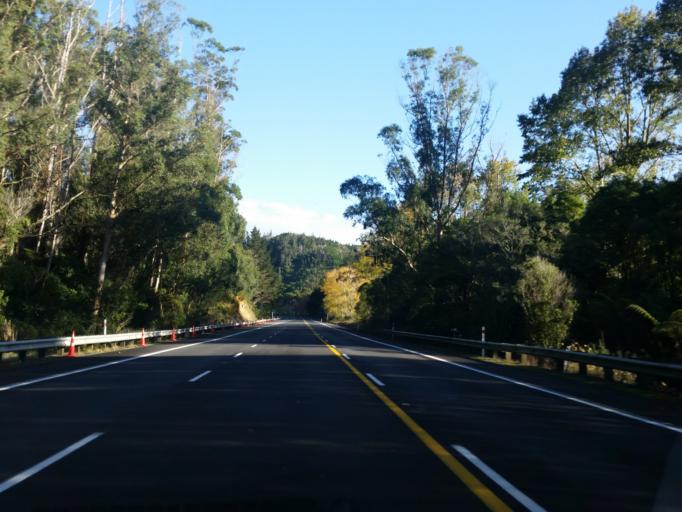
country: NZ
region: Bay of Plenty
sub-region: Western Bay of Plenty District
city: Waihi Beach
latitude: -37.4576
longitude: 175.9048
